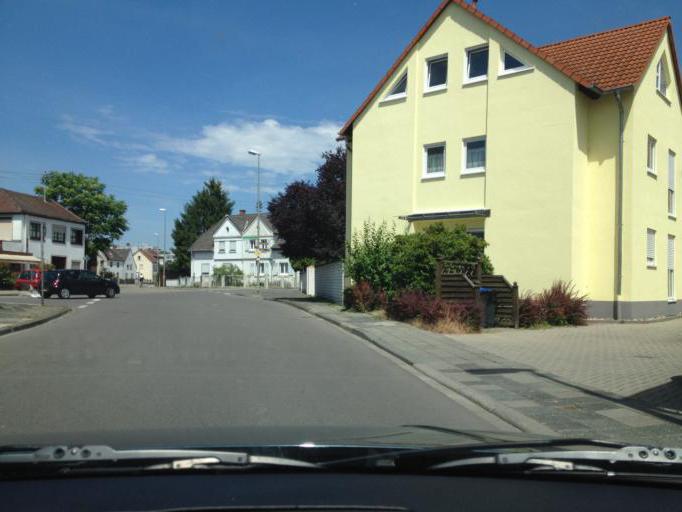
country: DE
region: Rheinland-Pfalz
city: Neuhofen
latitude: 49.4260
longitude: 8.4242
